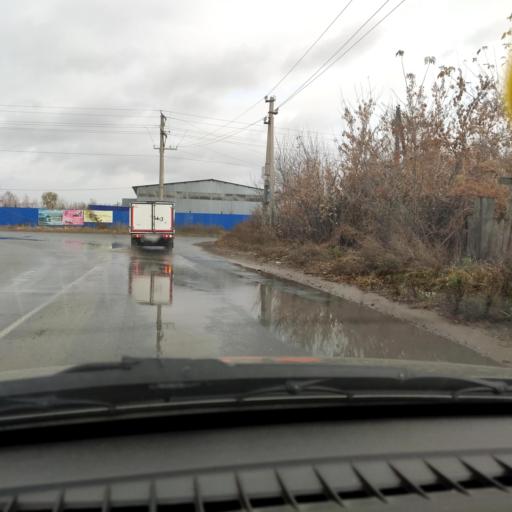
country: RU
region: Samara
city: Zhigulevsk
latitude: 53.5239
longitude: 49.4880
